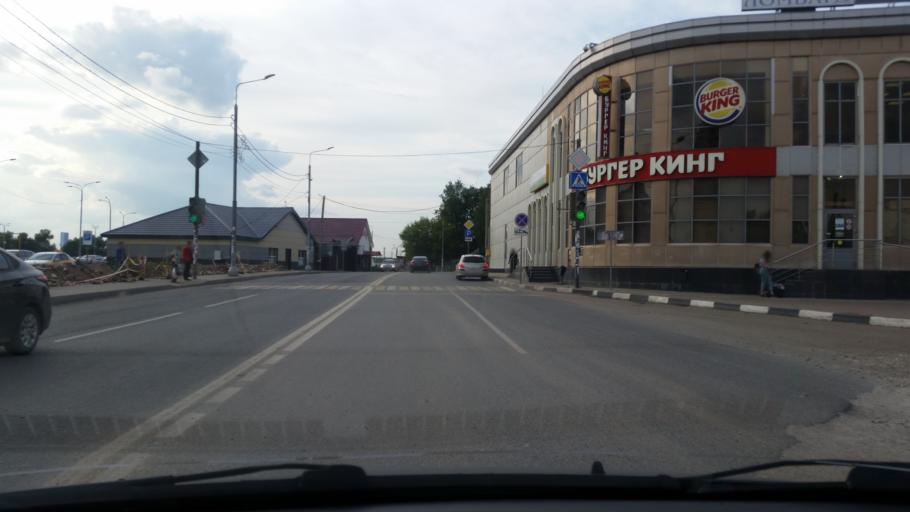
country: RU
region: Moskovskaya
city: Serpukhov
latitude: 54.9349
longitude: 37.4502
